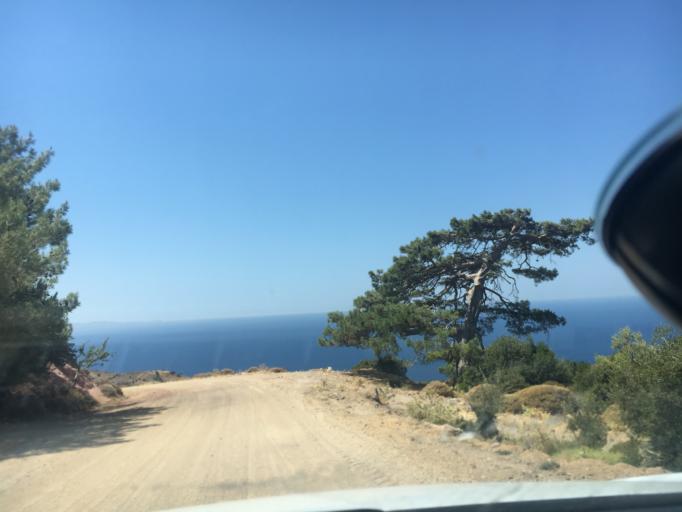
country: TR
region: Canakkale
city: Gulpinar
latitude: 39.4852
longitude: 26.0757
